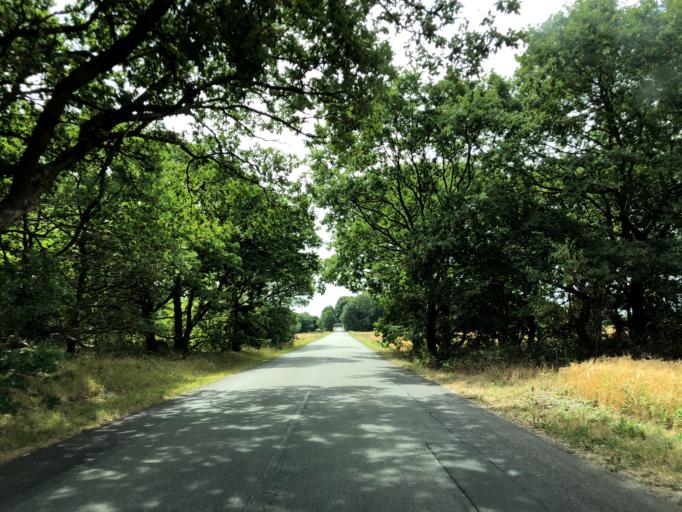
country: DK
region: South Denmark
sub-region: Vejle Kommune
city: Egtved
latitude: 55.6267
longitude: 9.1940
